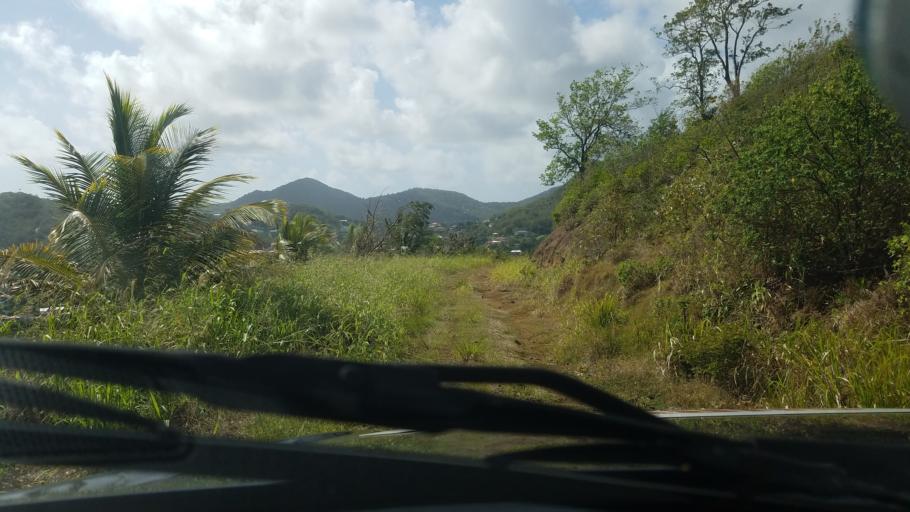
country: LC
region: Gros-Islet
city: Gros Islet
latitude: 14.0649
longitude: -60.9481
